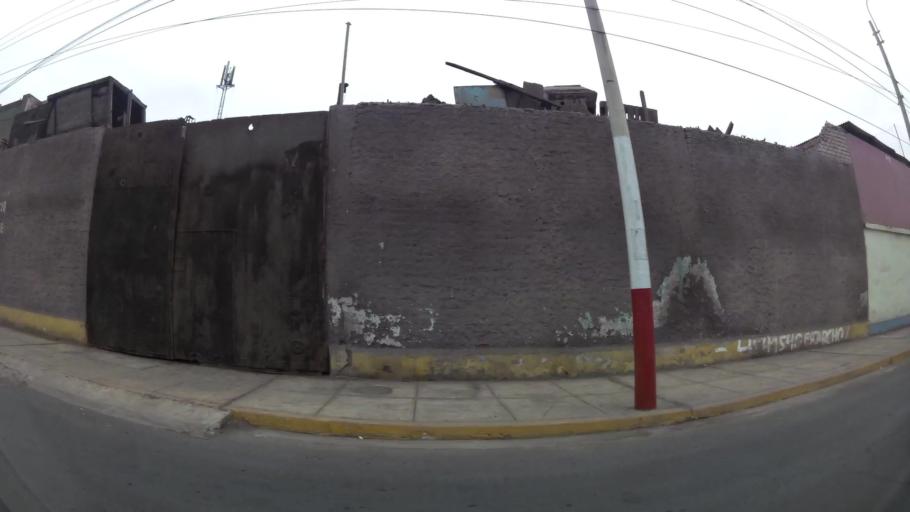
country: PE
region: Callao
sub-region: Callao
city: Callao
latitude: -12.0661
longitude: -77.1530
